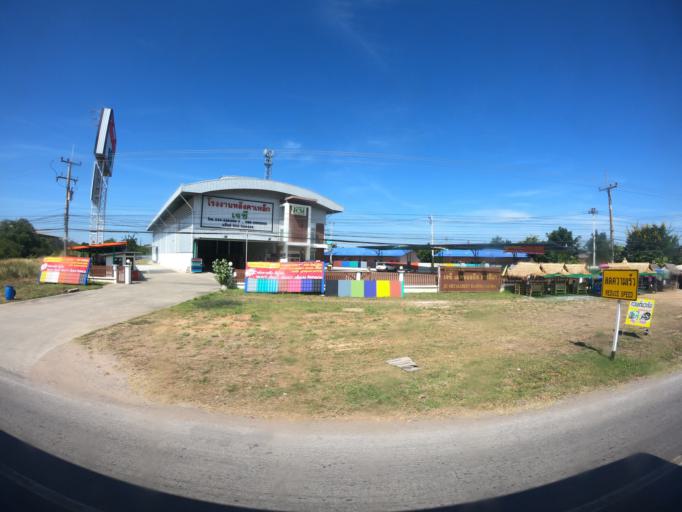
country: TH
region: Nakhon Ratchasima
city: Nakhon Ratchasima
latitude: 15.0380
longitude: 102.1464
